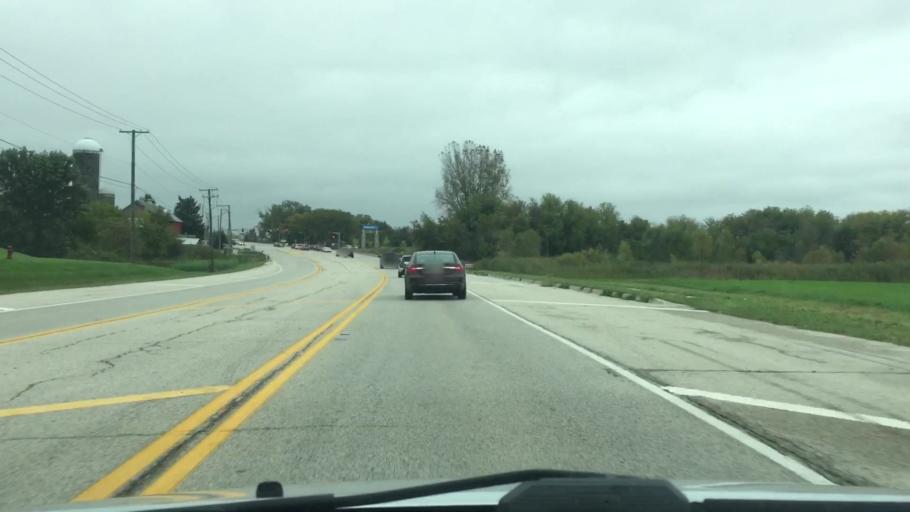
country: US
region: Illinois
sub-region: McHenry County
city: McCullom Lake
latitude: 42.3737
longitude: -88.2695
